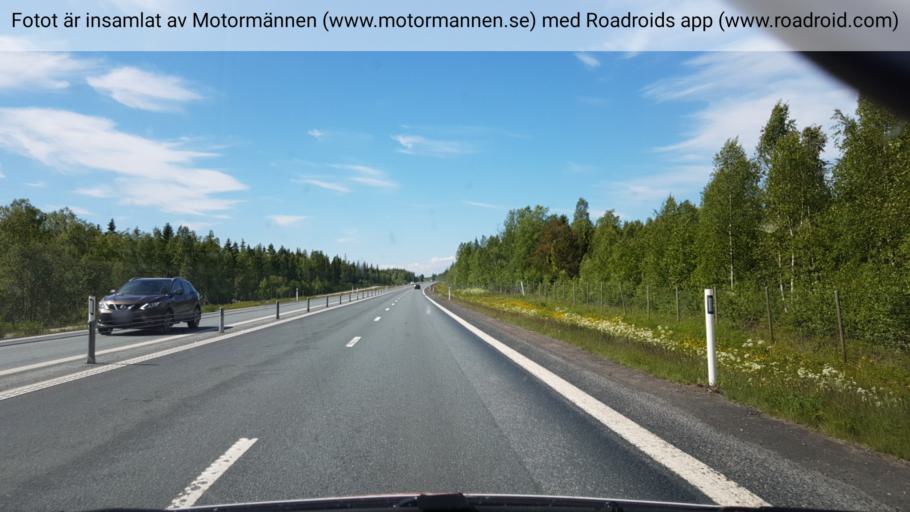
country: SE
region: Norrbotten
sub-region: Haparanda Kommun
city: Haparanda
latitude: 65.8091
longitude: 23.9742
